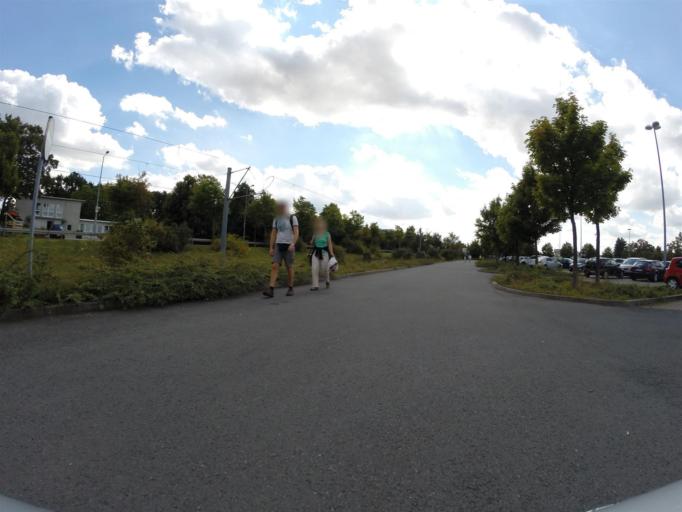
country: DE
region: Thuringia
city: Erfurt
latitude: 50.9644
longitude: 10.9970
